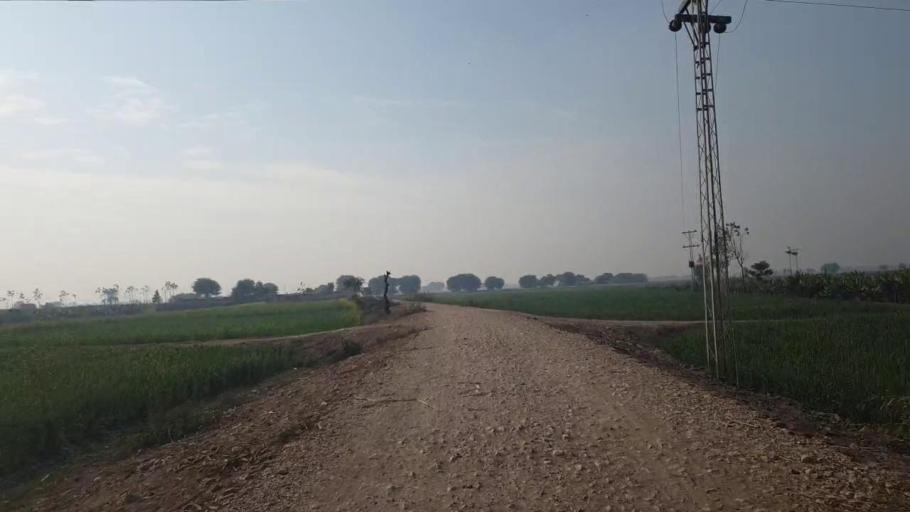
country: PK
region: Sindh
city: Tando Allahyar
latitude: 25.3824
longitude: 68.7692
